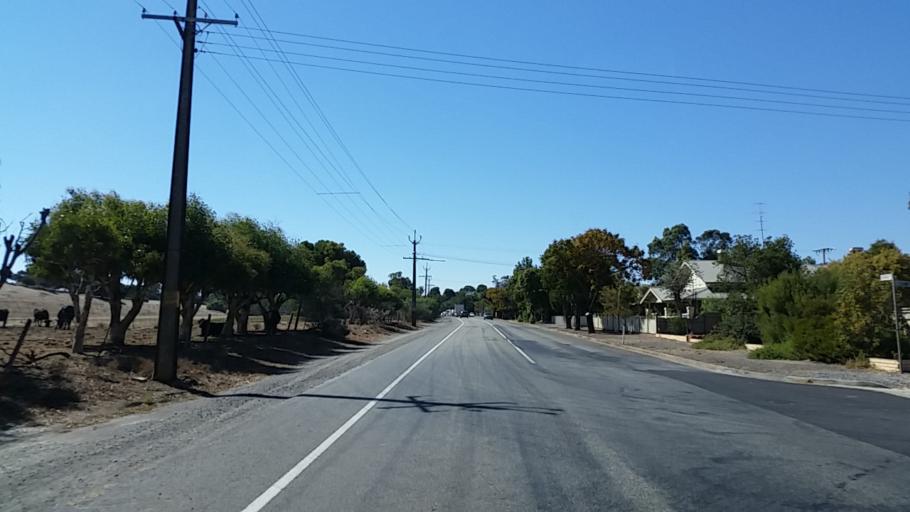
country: AU
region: South Australia
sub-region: Light
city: Kapunda
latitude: -34.0857
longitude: 138.7781
